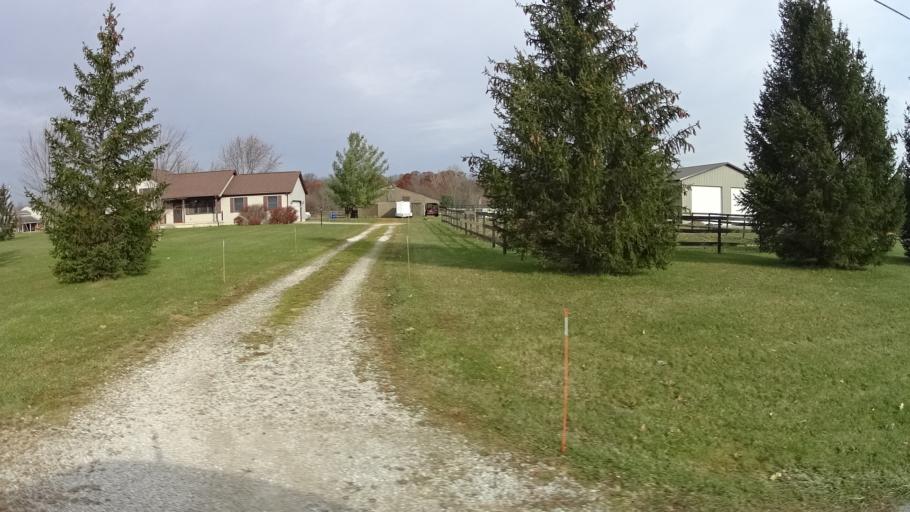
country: US
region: Ohio
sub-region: Lorain County
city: Wellington
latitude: 41.1368
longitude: -82.1314
